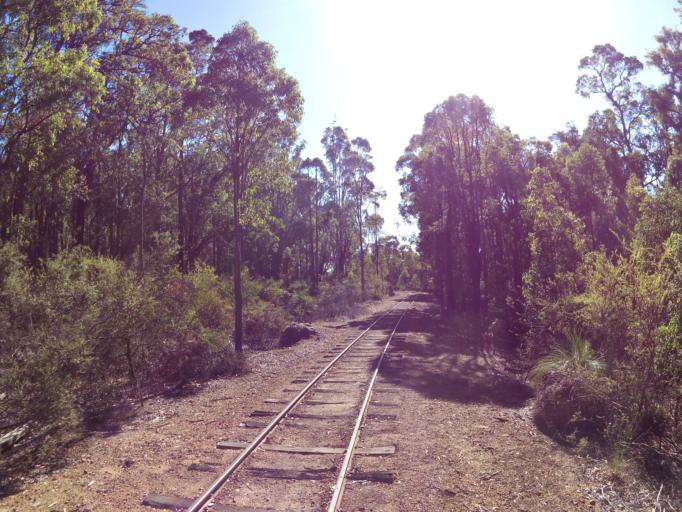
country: AU
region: Western Australia
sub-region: Waroona
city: Waroona
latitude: -32.7113
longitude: 116.0741
